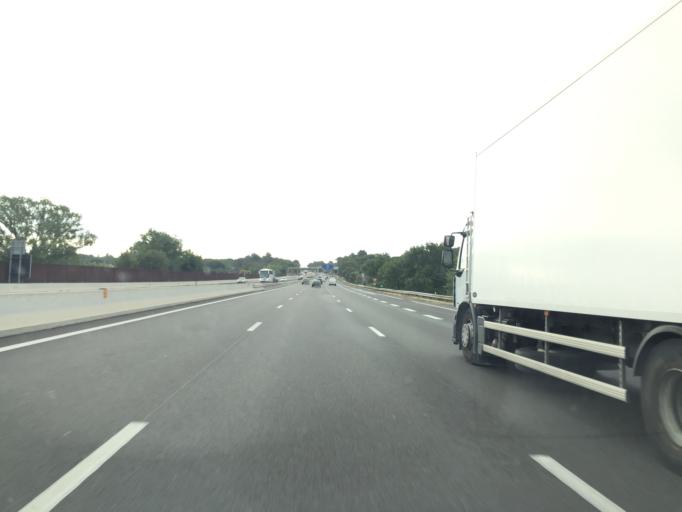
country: FR
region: Provence-Alpes-Cote d'Azur
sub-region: Departement du Var
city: Puget-sur-Argens
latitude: 43.4633
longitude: 6.6795
